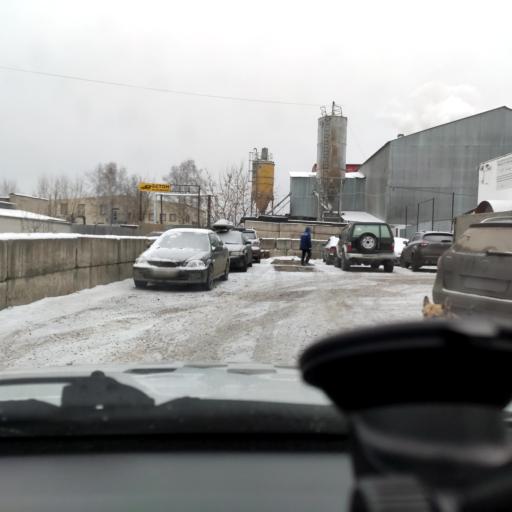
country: RU
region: Perm
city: Kondratovo
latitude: 58.0060
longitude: 56.1404
